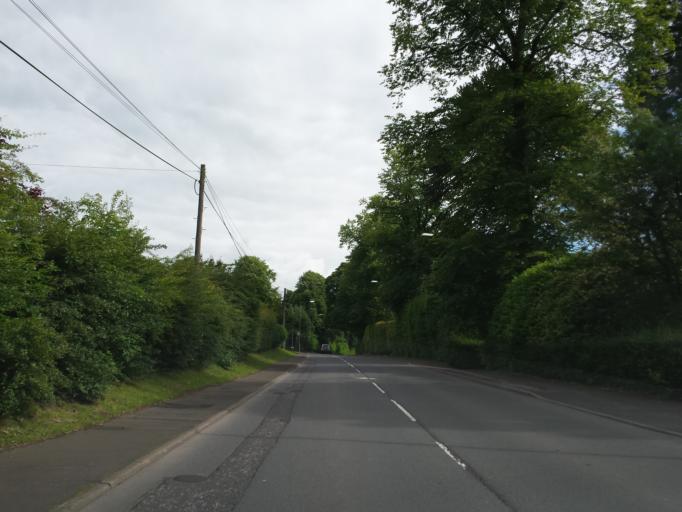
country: GB
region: Scotland
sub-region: Dumfries and Galloway
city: Moffat
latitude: 55.3263
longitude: -3.4472
